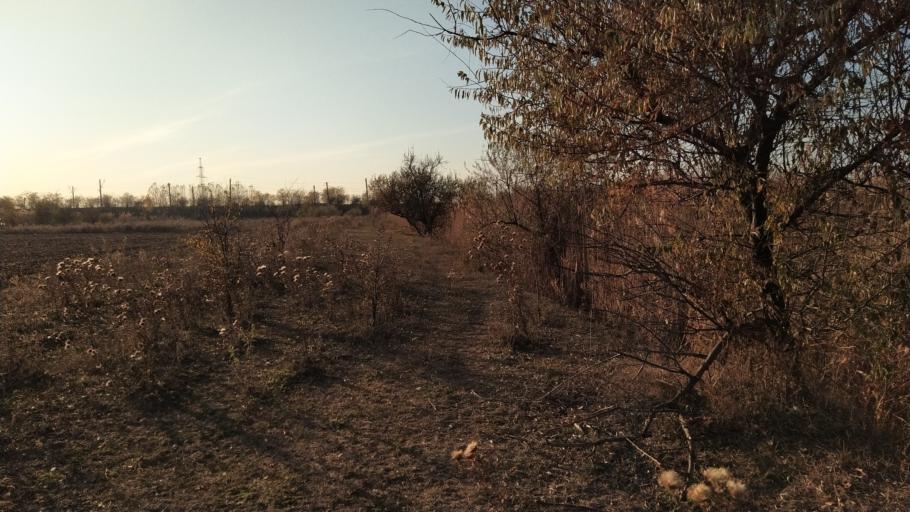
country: RU
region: Rostov
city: Bataysk
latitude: 47.1216
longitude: 39.7167
